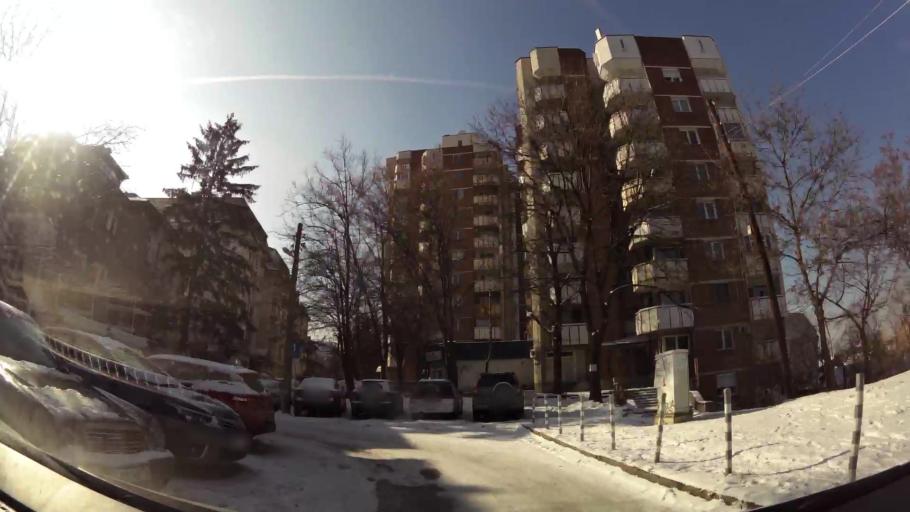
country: BG
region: Sofia-Capital
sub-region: Stolichna Obshtina
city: Sofia
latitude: 42.6731
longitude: 23.3159
